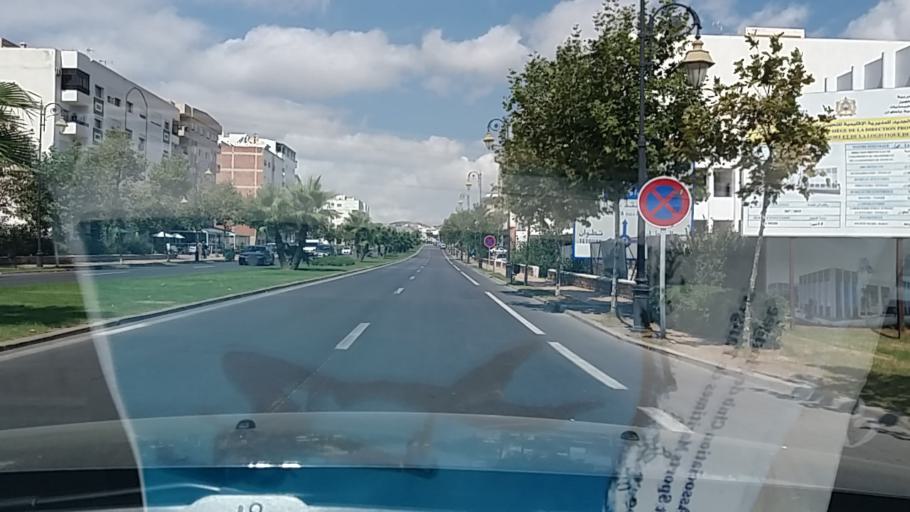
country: MA
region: Tanger-Tetouan
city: Tetouan
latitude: 35.5884
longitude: -5.3342
